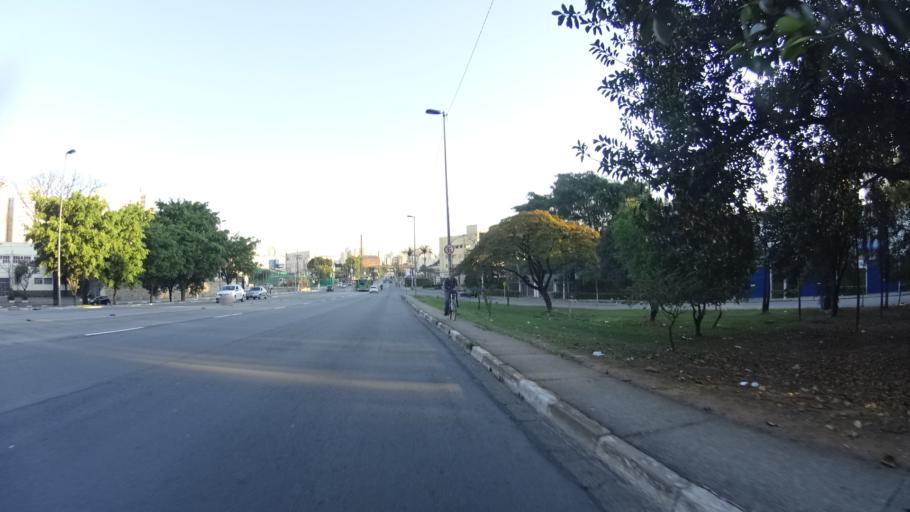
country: BR
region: Sao Paulo
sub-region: Sao Paulo
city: Sao Paulo
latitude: -23.5108
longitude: -46.6901
